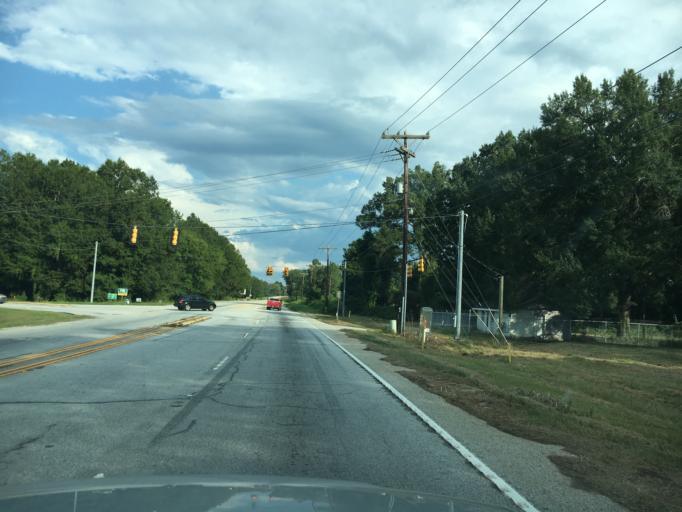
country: US
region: South Carolina
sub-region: Greenwood County
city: Ninety Six
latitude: 34.2382
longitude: -82.0691
